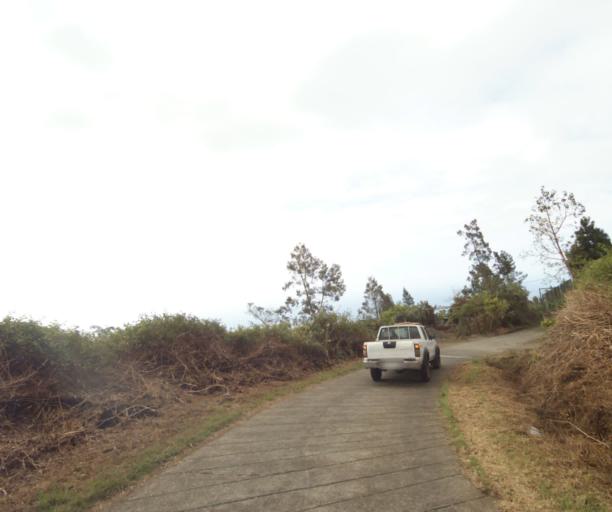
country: RE
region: Reunion
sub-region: Reunion
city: Saint-Paul
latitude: -21.0118
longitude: 55.3482
